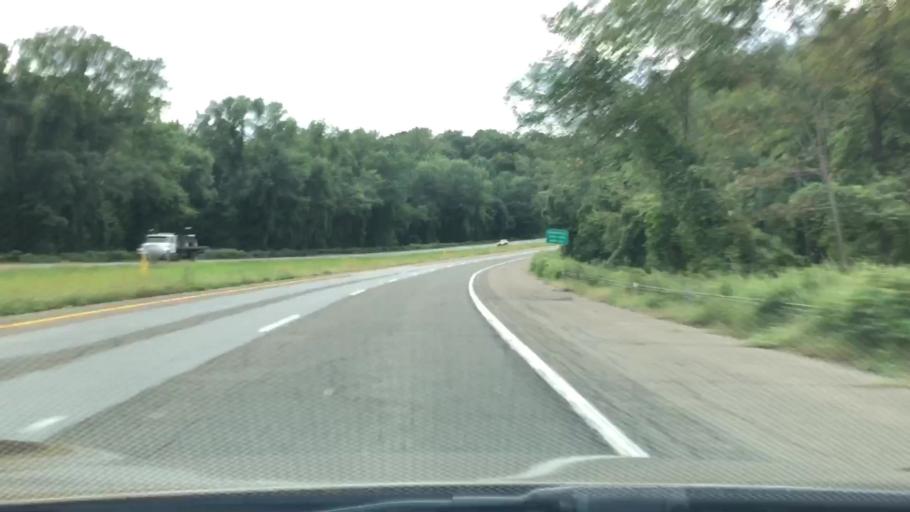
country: US
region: New York
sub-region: Westchester County
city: Briarcliff Manor
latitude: 41.1159
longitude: -73.8282
